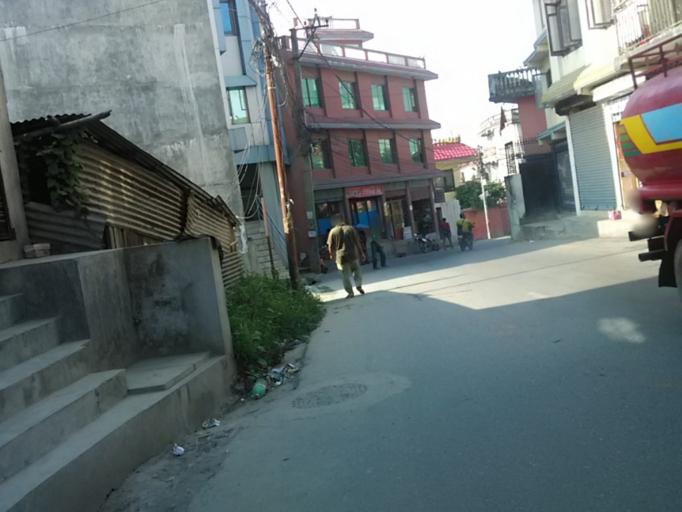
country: NP
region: Central Region
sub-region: Bagmati Zone
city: Kathmandu
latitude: 27.7248
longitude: 85.3409
